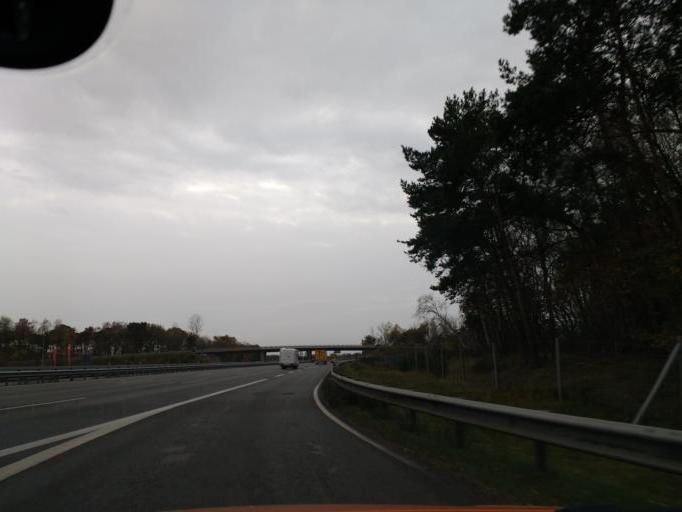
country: DE
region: Lower Saxony
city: Ottersberg
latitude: 53.0887
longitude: 9.1760
